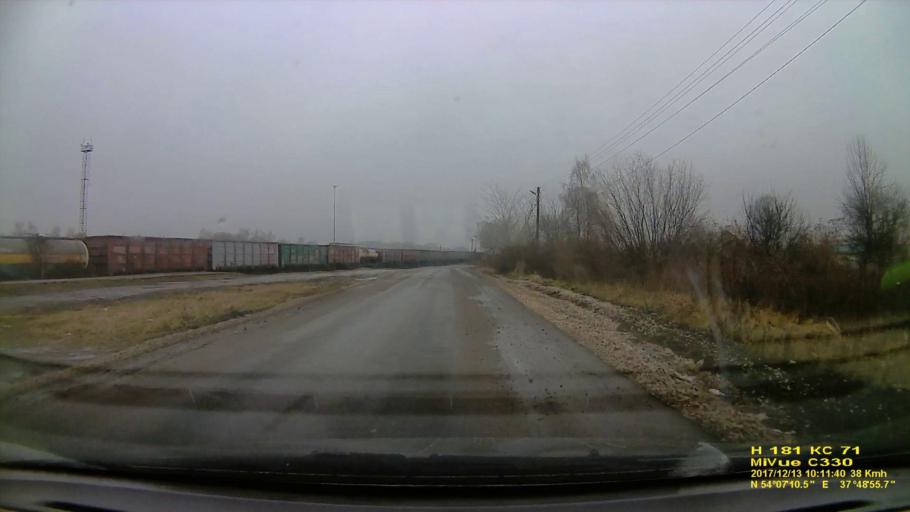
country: RU
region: Tula
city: Bolokhovo
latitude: 54.1196
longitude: 37.8154
